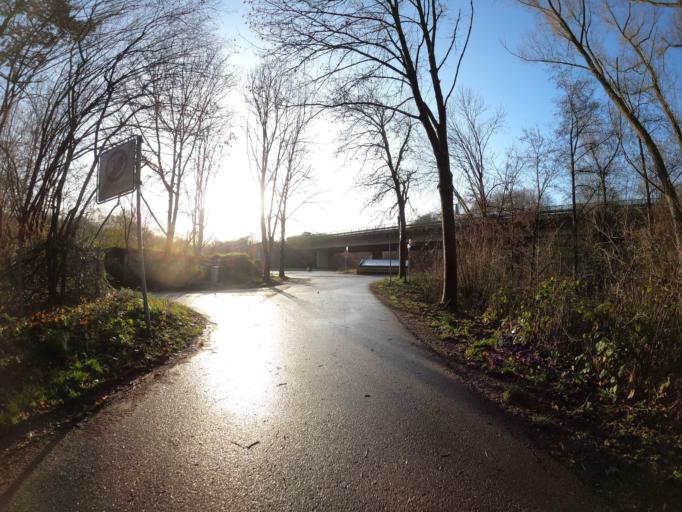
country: DE
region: Baden-Wuerttemberg
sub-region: Regierungsbezirk Stuttgart
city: Wangen
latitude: 48.7028
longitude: 9.6144
